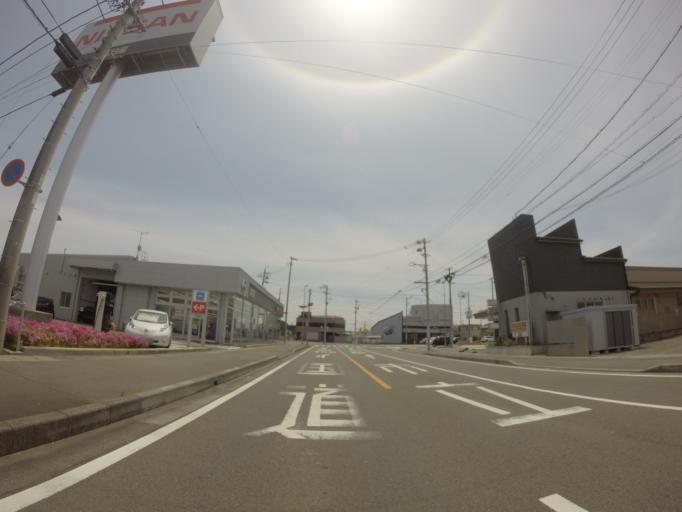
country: JP
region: Shizuoka
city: Yaizu
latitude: 34.8377
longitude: 138.3091
